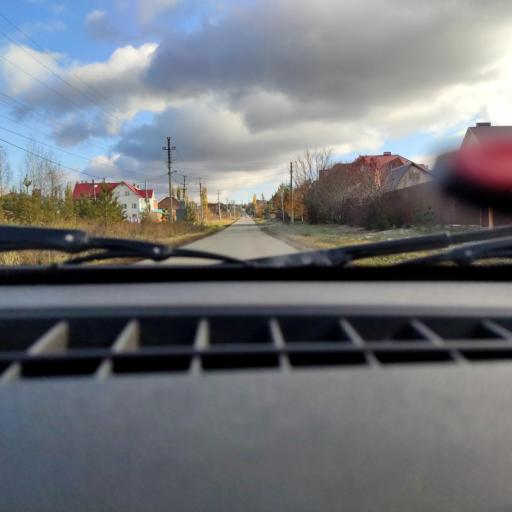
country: RU
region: Bashkortostan
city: Ufa
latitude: 54.5990
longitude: 55.9312
